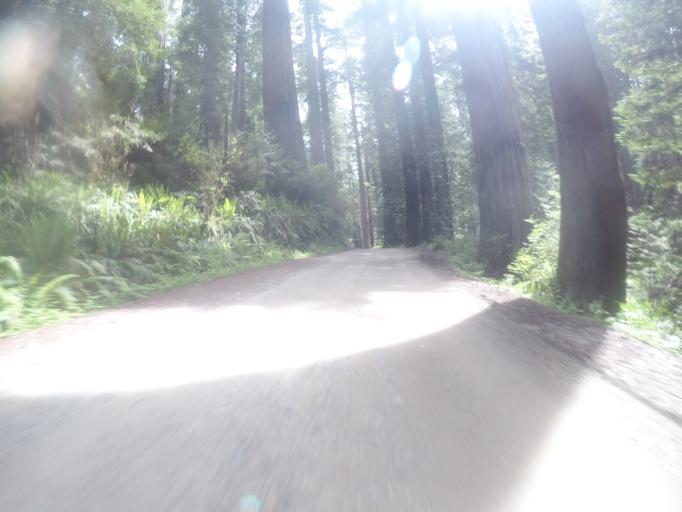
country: US
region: California
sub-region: Del Norte County
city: Bertsch-Oceanview
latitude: 41.7632
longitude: -124.1326
